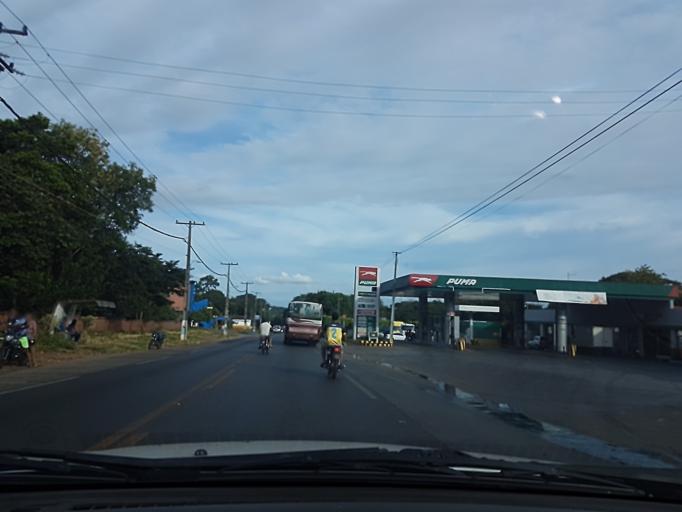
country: PY
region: Central
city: San Lorenzo
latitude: -25.2805
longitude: -57.4726
